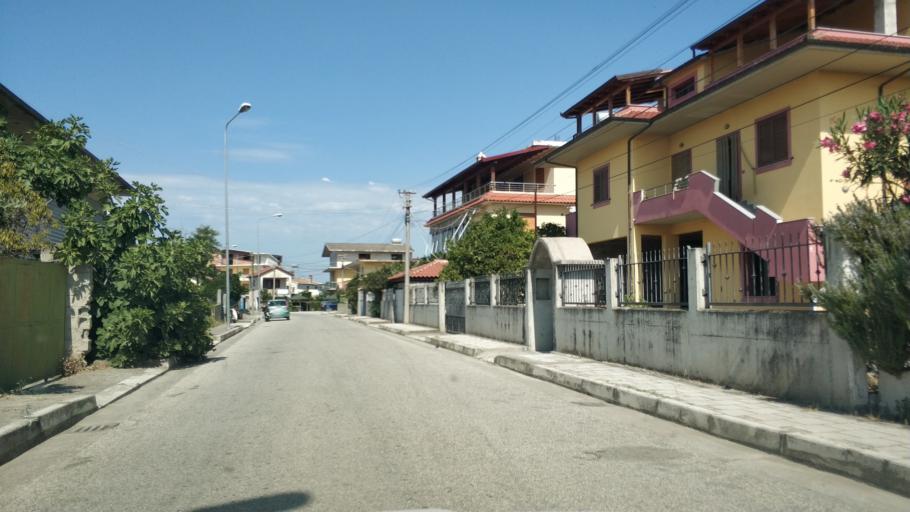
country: AL
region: Fier
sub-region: Rrethi i Lushnjes
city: Divjake
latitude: 40.9978
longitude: 19.5275
